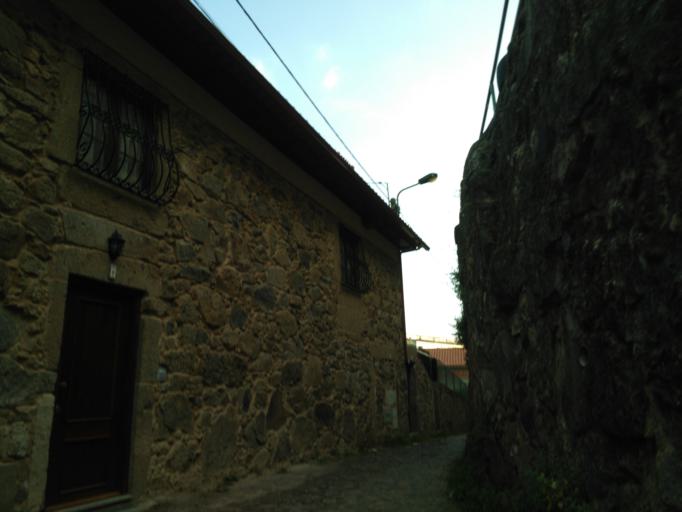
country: PT
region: Braga
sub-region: Braga
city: Braga
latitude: 41.5446
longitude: -8.4153
